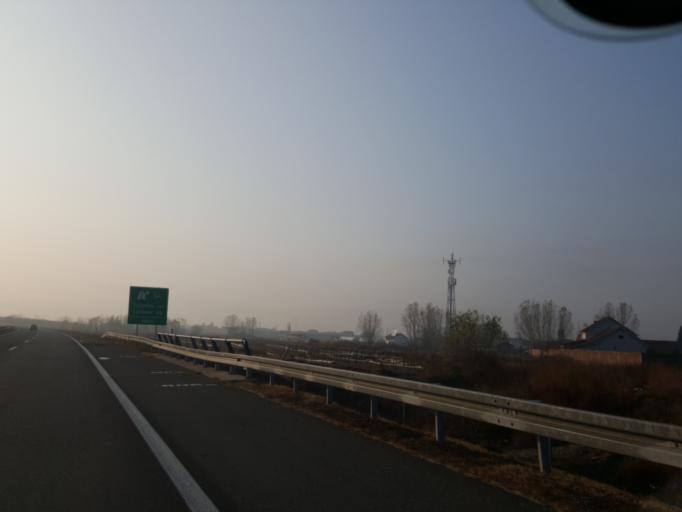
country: RS
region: Central Serbia
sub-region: Jablanicki Okrug
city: Leskovac
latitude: 42.9864
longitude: 22.0282
